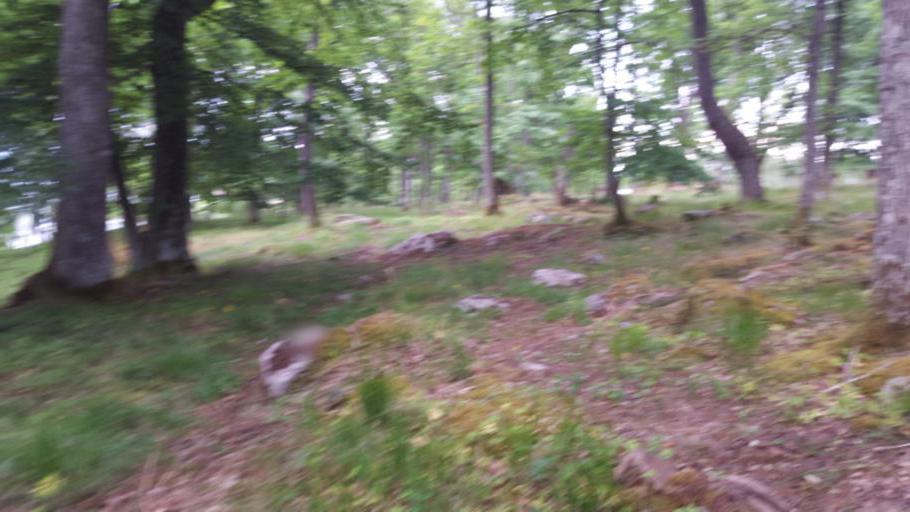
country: SE
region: Joenkoeping
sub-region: Varnamo Kommun
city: Bor
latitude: 57.0371
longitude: 14.1766
